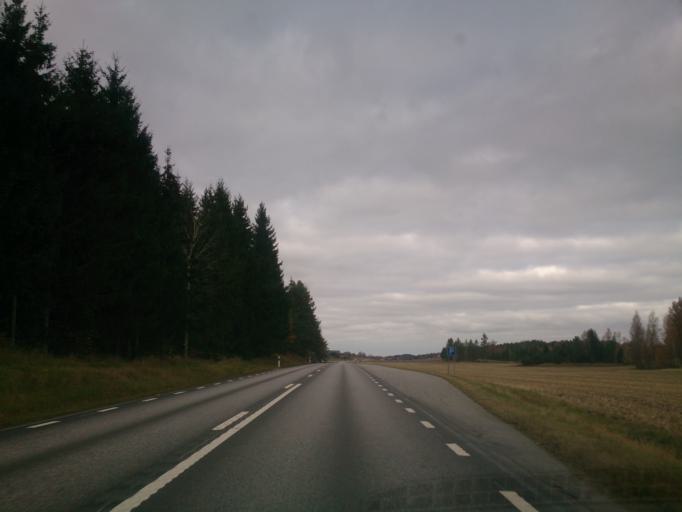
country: SE
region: OEstergoetland
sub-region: Linkopings Kommun
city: Sturefors
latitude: 58.3289
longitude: 15.8565
